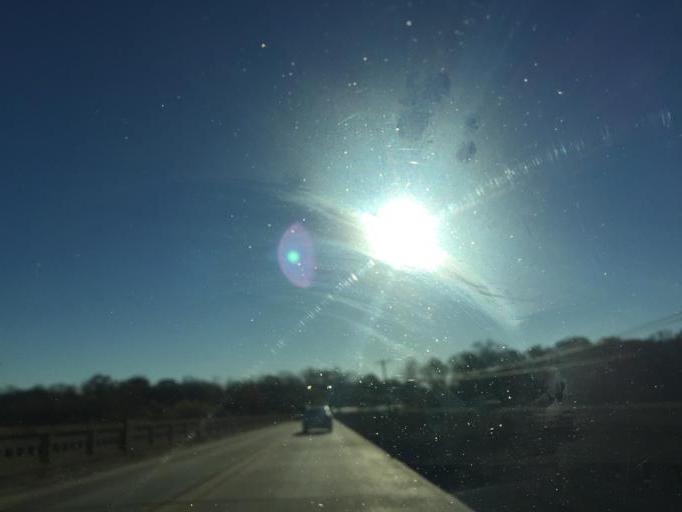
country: US
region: Mississippi
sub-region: Hinds County
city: Jackson
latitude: 32.2892
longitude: -90.1783
